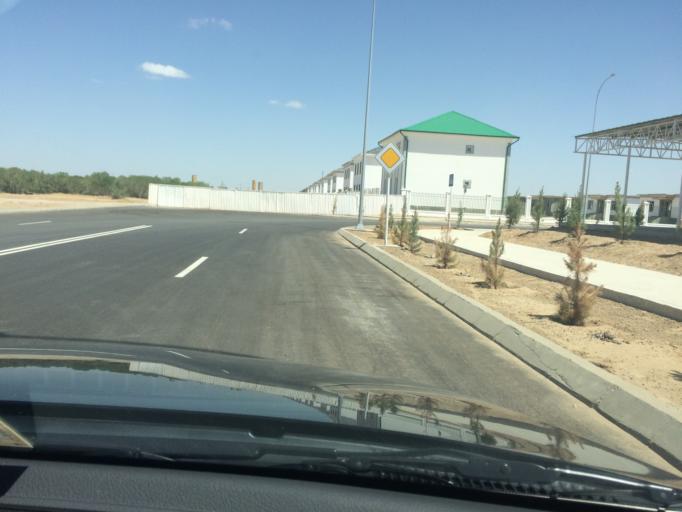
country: TM
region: Ahal
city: Abadan
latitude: 38.1001
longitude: 58.2934
